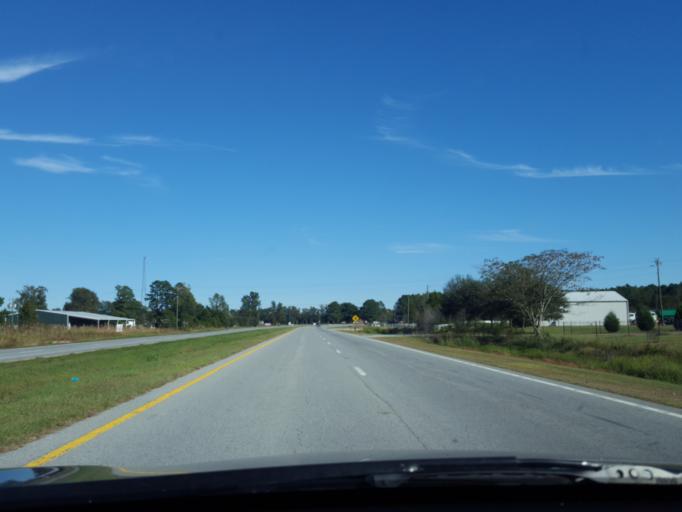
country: US
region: North Carolina
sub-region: Beaufort County
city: Washington
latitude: 35.6252
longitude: -77.1836
